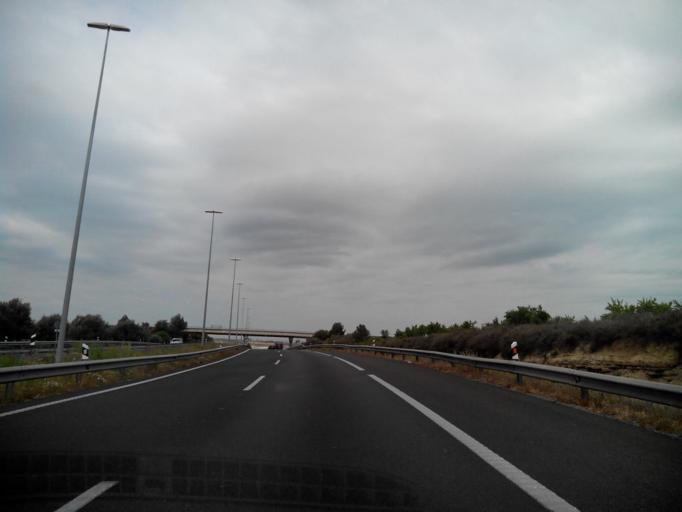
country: ES
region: Catalonia
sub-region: Provincia de Lleida
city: Tarrega
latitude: 41.6576
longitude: 1.1619
